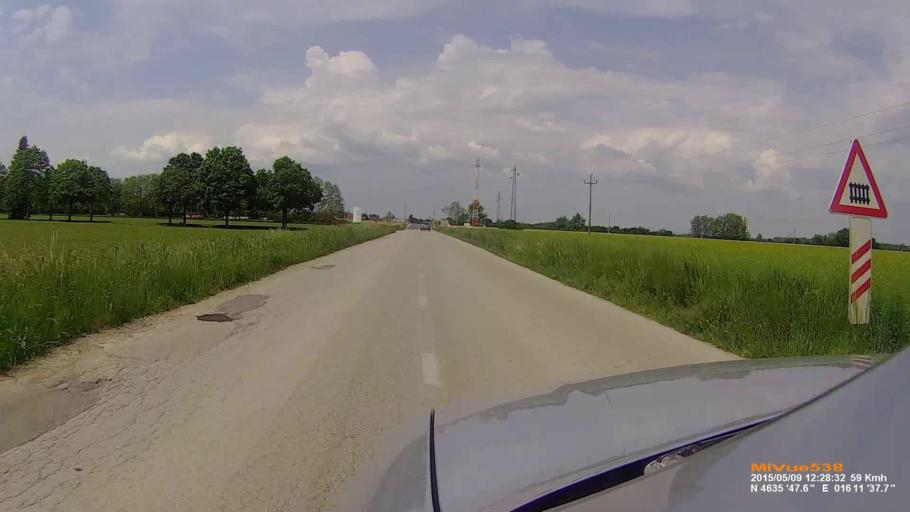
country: SI
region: Verzej
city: Verzej
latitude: 46.5966
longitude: 16.1939
